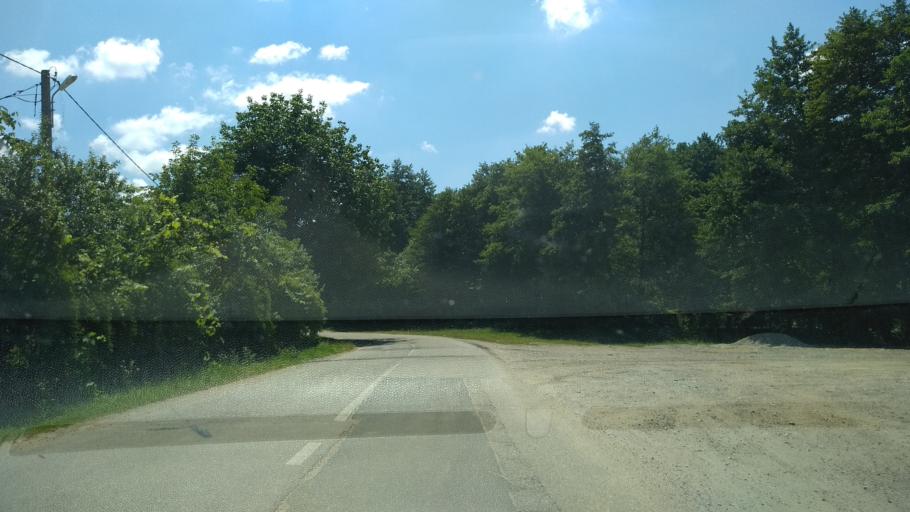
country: RO
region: Hunedoara
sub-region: Comuna Orastioara de Sus
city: Orastioara de Sus
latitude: 45.6949
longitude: 23.1618
